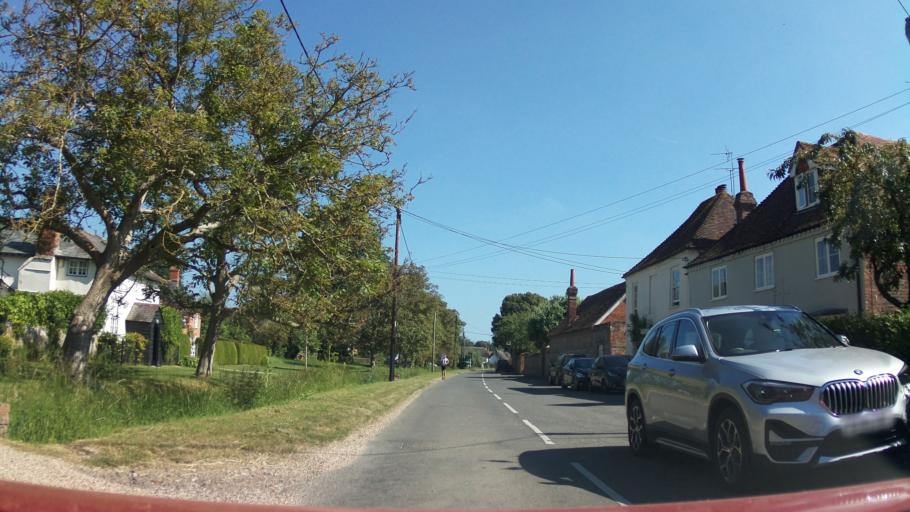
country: GB
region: England
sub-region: Hampshire
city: Abbotts Ann
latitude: 51.2393
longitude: -1.5667
